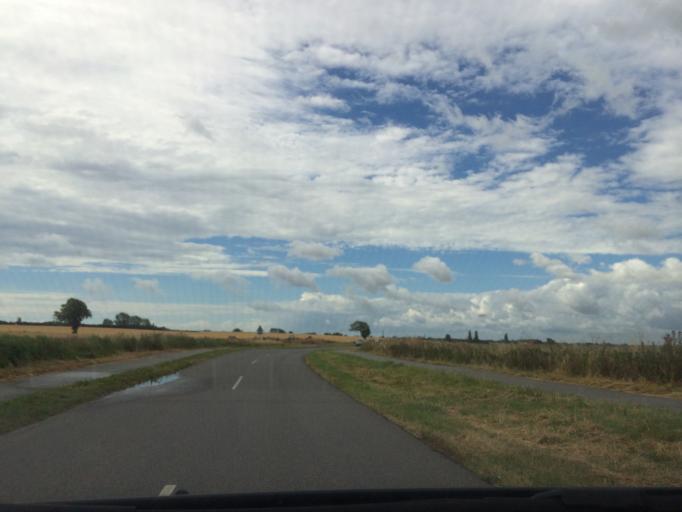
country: DK
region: Zealand
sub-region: Vordingborg Kommune
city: Stege
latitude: 55.0198
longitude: 12.2901
